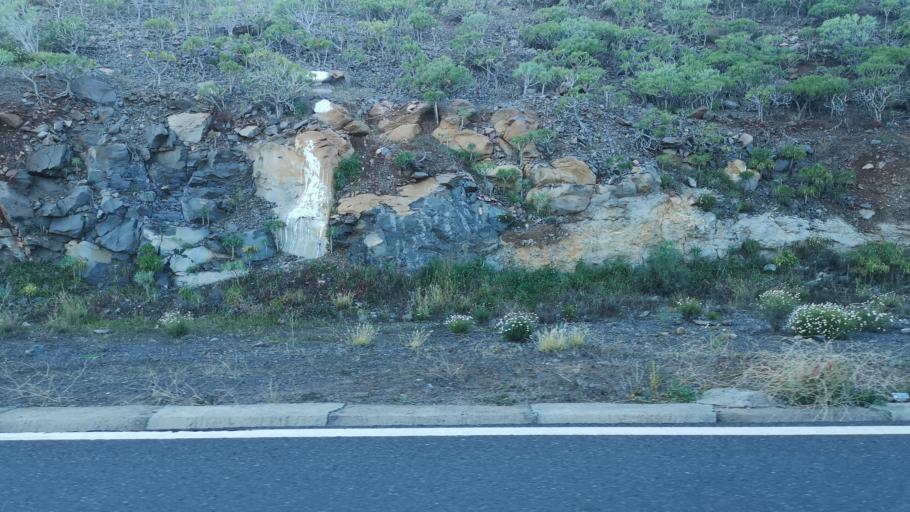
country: ES
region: Canary Islands
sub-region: Provincia de Santa Cruz de Tenerife
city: San Sebastian de la Gomera
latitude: 28.0817
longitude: -17.1290
